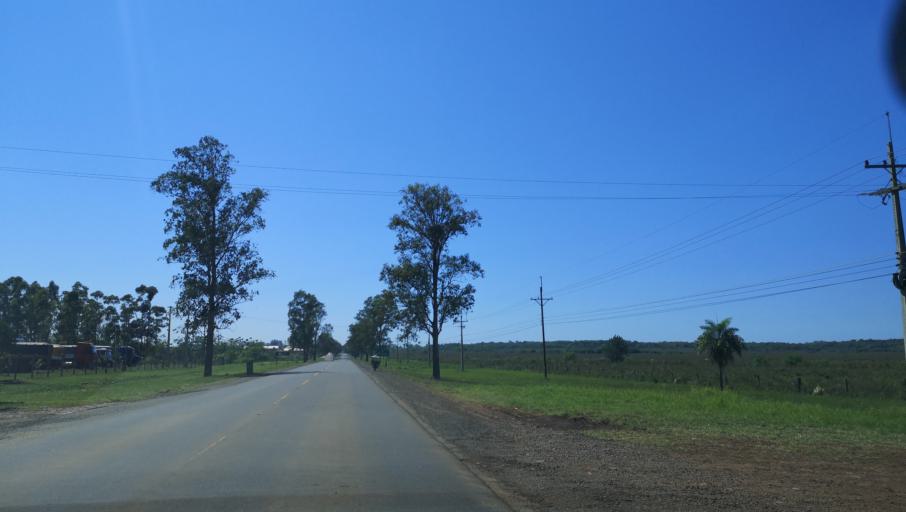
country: PY
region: Itapua
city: Carmen del Parana
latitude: -27.2205
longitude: -56.1310
